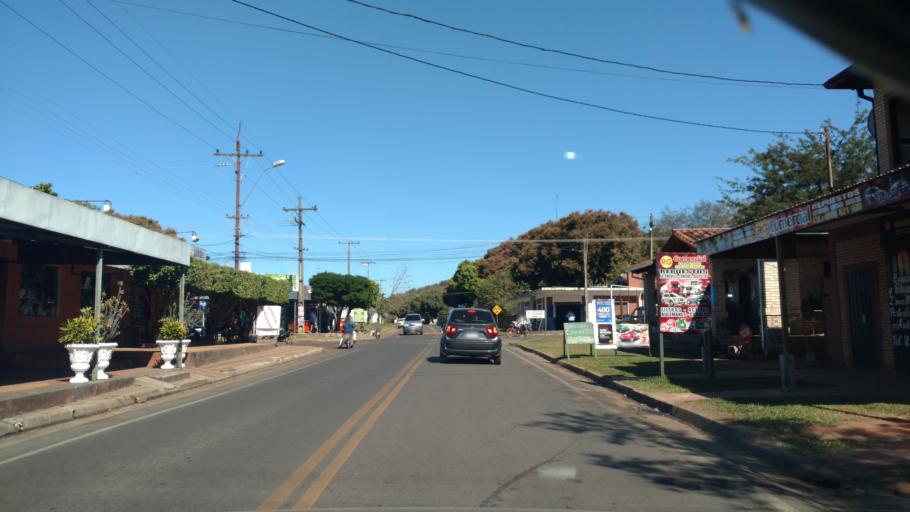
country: PY
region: Paraguari
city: Pirayu
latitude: -25.4870
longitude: -57.2359
